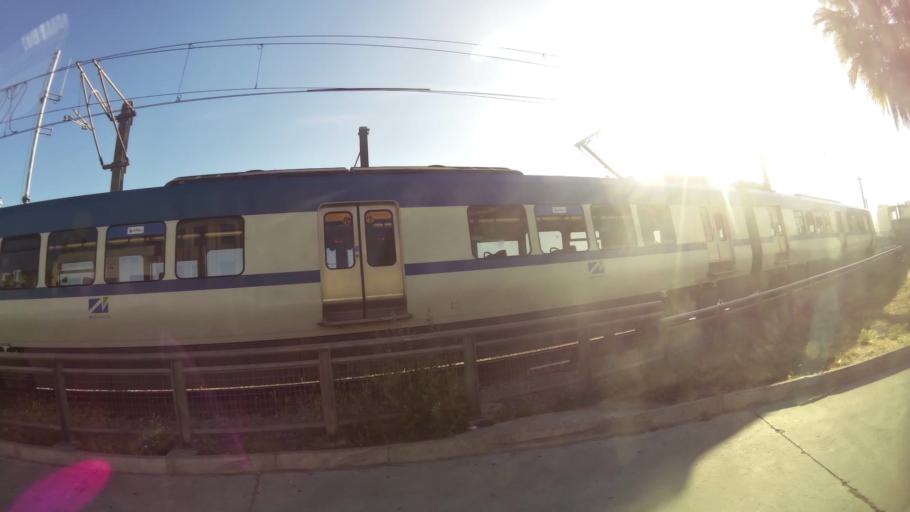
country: CL
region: Valparaiso
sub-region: Provincia de Valparaiso
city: Valparaiso
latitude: -33.0398
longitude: -71.6256
